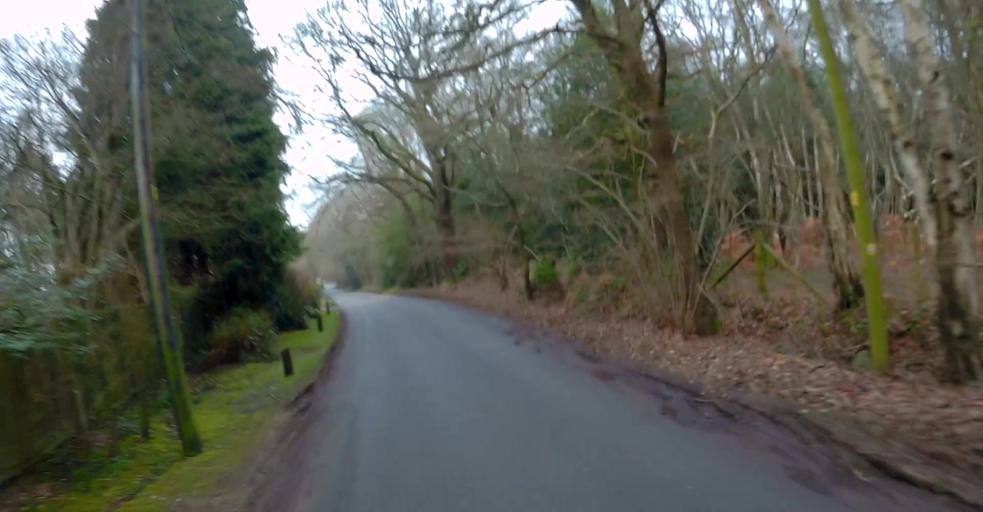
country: GB
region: England
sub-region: Hampshire
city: Eversley
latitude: 51.3728
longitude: -0.8833
